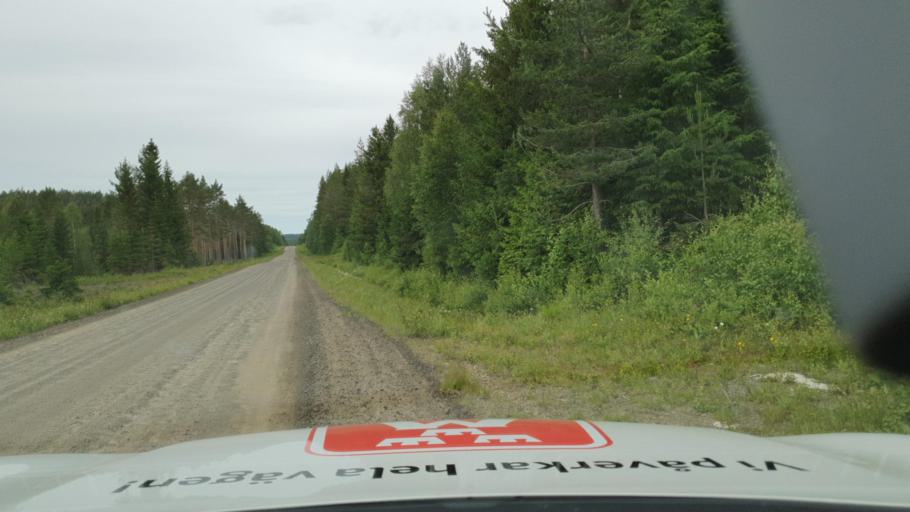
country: SE
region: Vaesterbotten
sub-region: Skelleftea Kommun
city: Burtraesk
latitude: 64.3248
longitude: 20.6333
